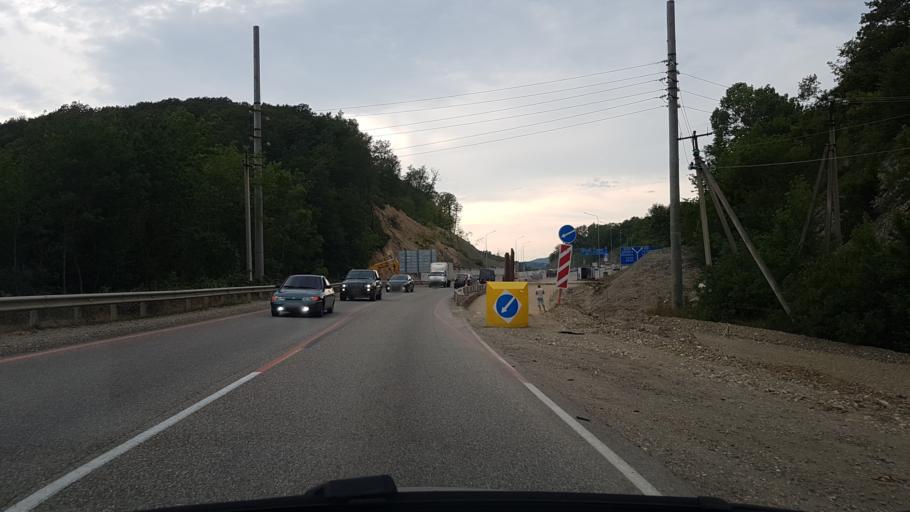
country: RU
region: Krasnodarskiy
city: Dzhubga
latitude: 44.3619
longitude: 38.7145
